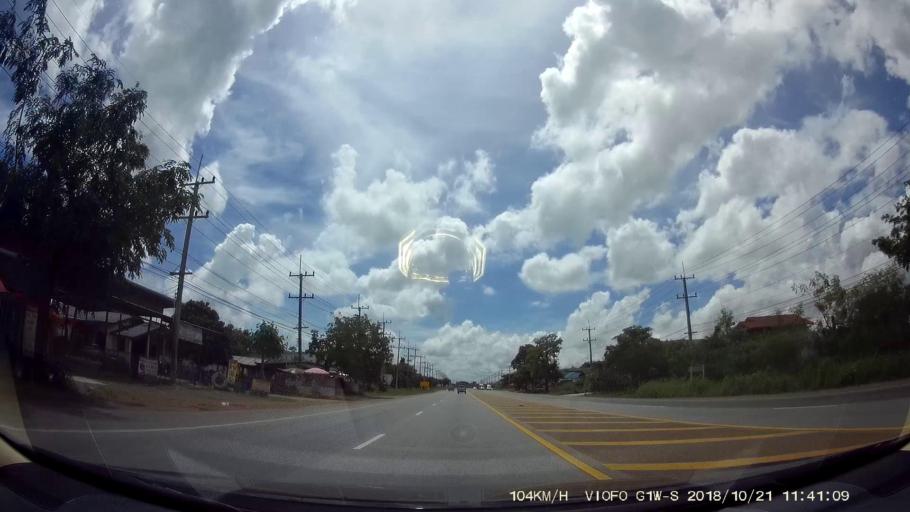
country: TH
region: Chaiyaphum
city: Chaiyaphum
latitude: 15.7033
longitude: 102.0149
